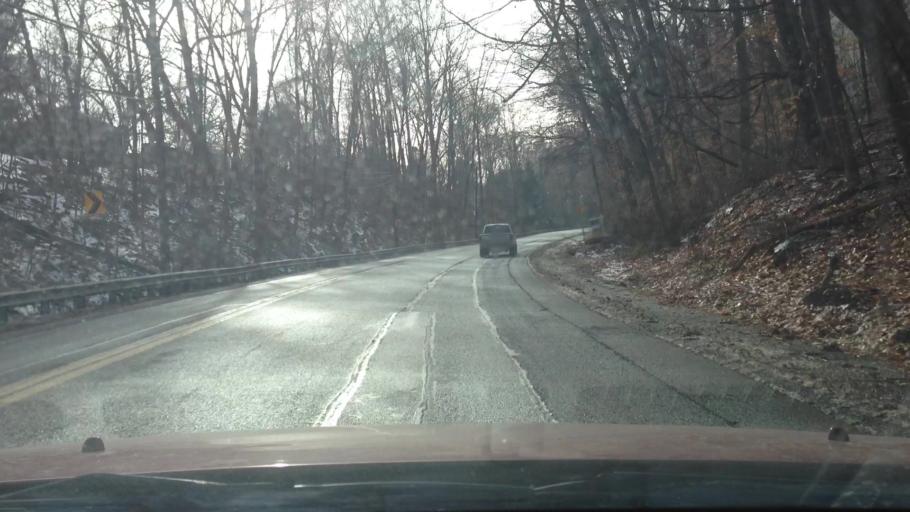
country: US
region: Pennsylvania
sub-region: Montgomery County
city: Narberth
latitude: 40.0373
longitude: -75.2542
